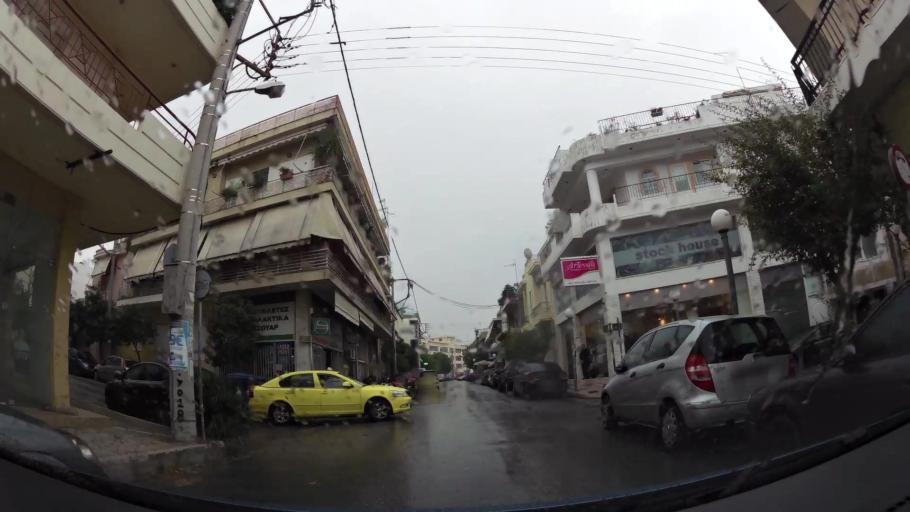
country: GR
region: Attica
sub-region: Nomarchia Athinas
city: Dhafni
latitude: 37.9544
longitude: 23.7408
